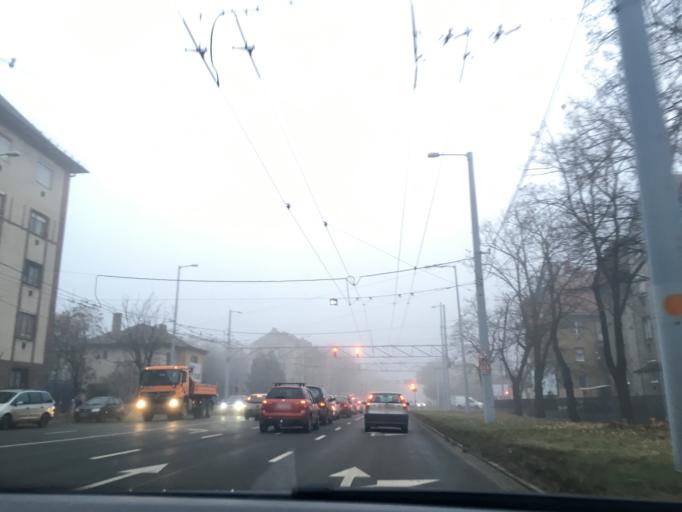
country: HU
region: Hajdu-Bihar
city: Debrecen
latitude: 47.5308
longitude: 21.6395
